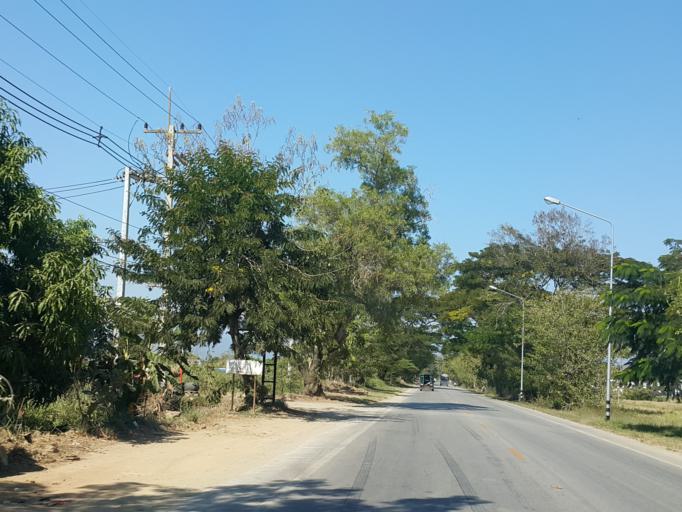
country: TH
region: Chiang Mai
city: Mae Taeng
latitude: 19.0575
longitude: 98.9594
